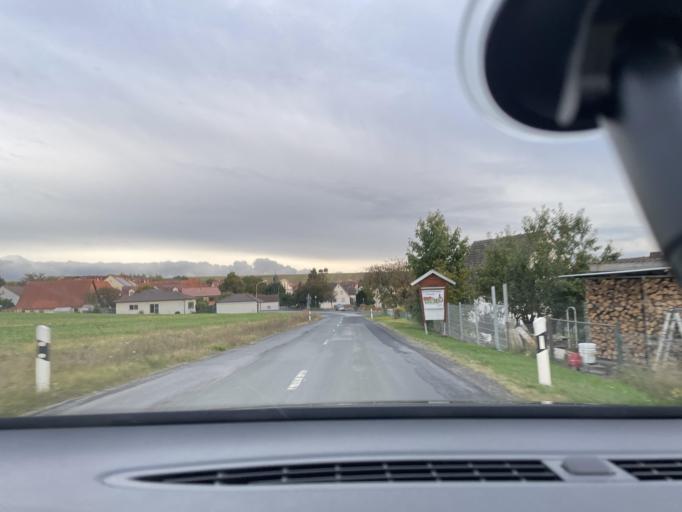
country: DE
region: Bavaria
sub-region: Regierungsbezirk Unterfranken
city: Rodelmaier
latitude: 50.3182
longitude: 10.2543
